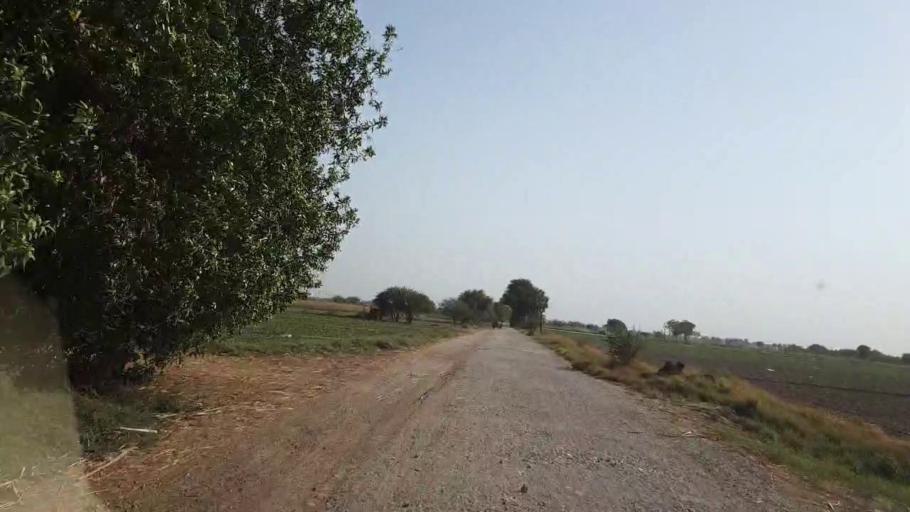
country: PK
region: Sindh
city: Tando Ghulam Ali
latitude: 25.0786
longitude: 68.8369
